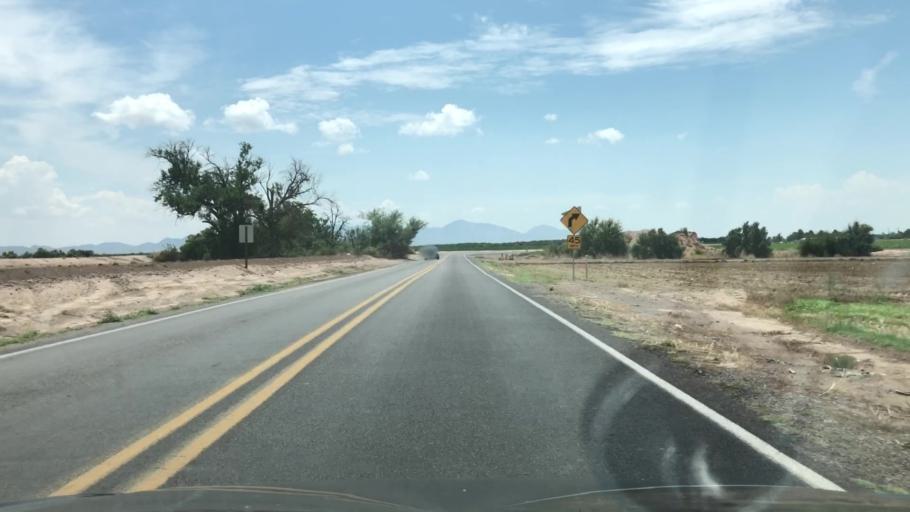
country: US
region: New Mexico
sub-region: Dona Ana County
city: Vado
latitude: 32.0697
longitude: -106.6816
